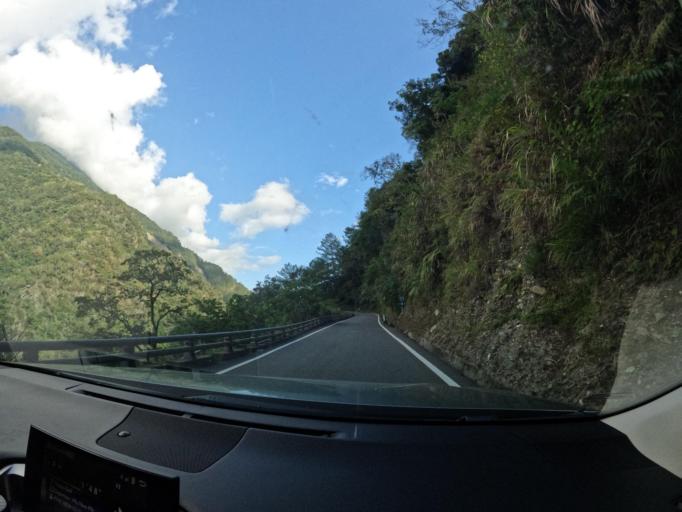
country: TW
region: Taiwan
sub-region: Taitung
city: Taitung
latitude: 23.1703
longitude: 121.0446
